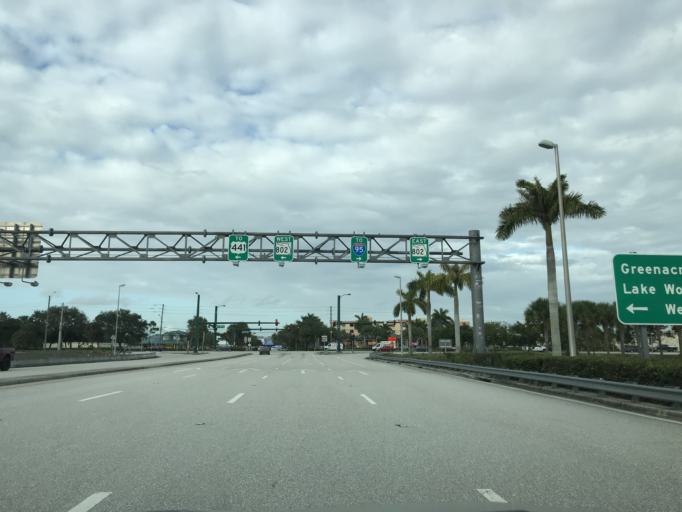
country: US
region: Florida
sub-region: Palm Beach County
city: Greenacres City
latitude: 26.6161
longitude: -80.1754
